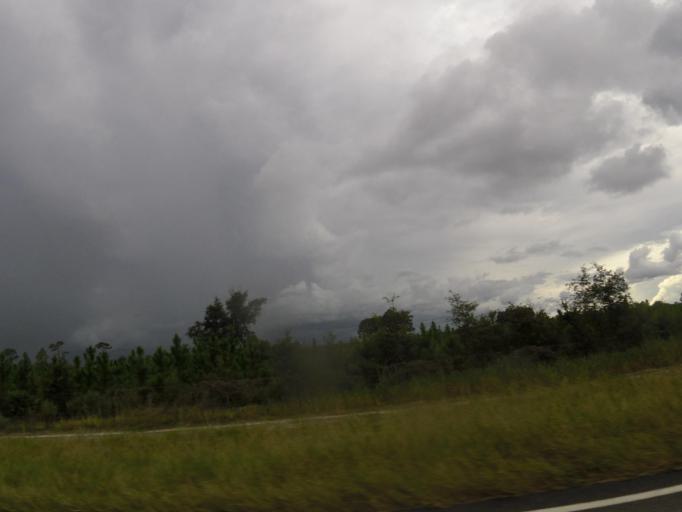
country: US
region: Florida
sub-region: Baker County
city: Macclenny
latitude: 30.4329
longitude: -82.1982
